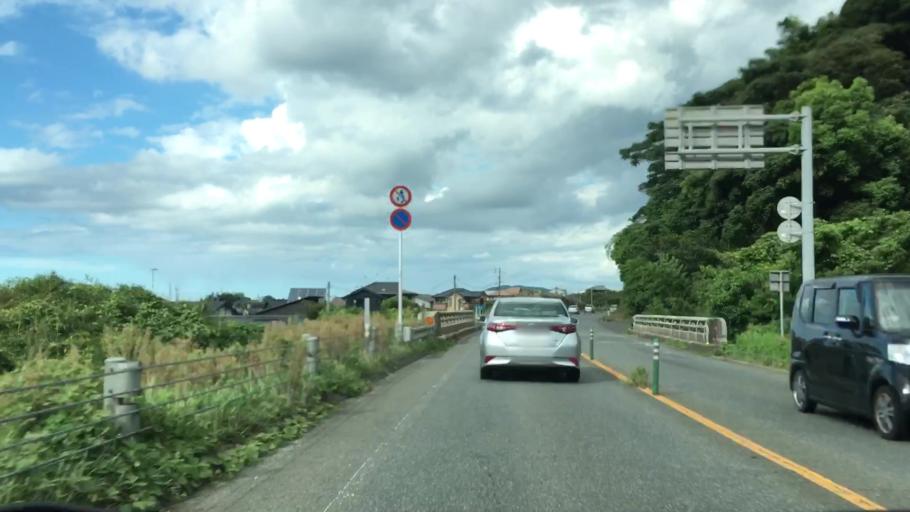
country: JP
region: Saga Prefecture
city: Karatsu
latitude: 33.4986
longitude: 130.0814
